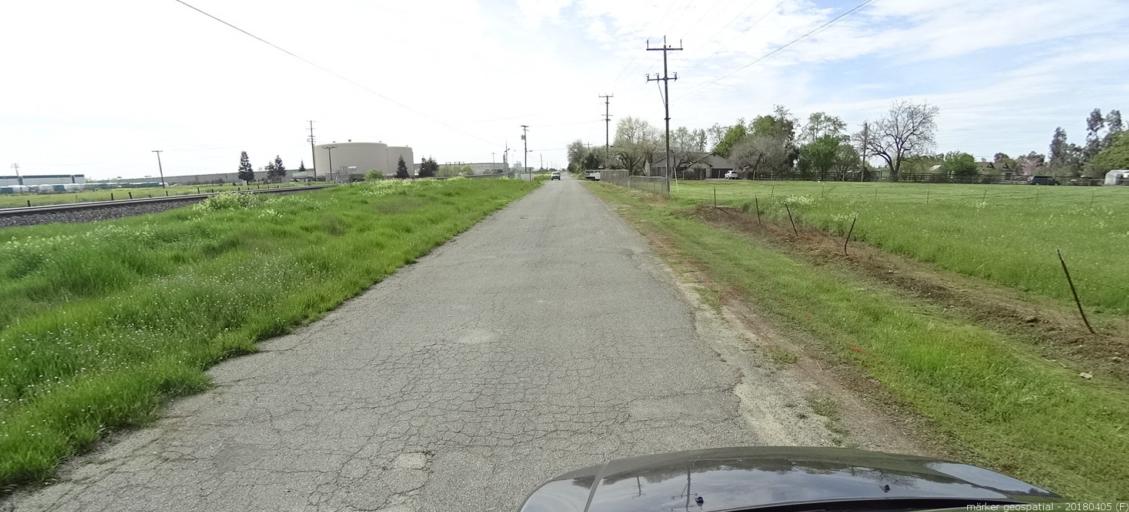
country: US
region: California
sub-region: Sacramento County
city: Galt
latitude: 38.2750
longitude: -121.3151
